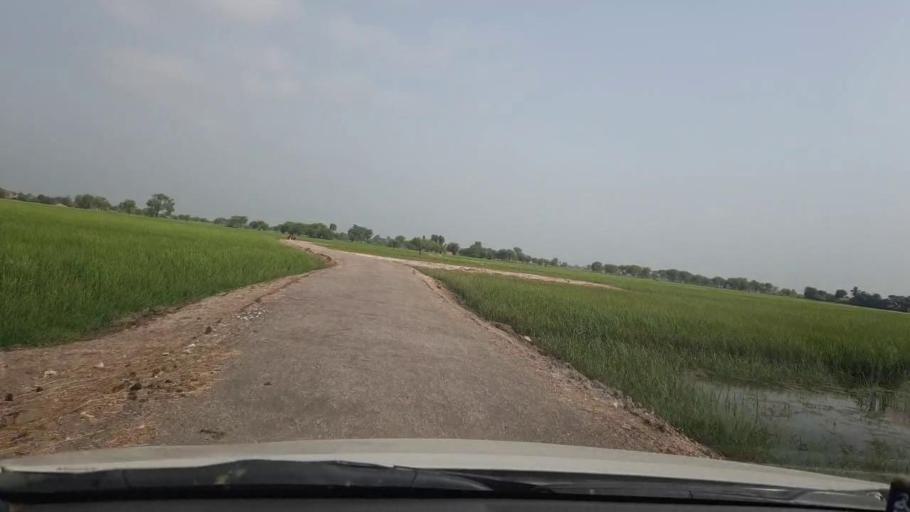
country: PK
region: Sindh
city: Shikarpur
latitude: 27.9913
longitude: 68.6068
